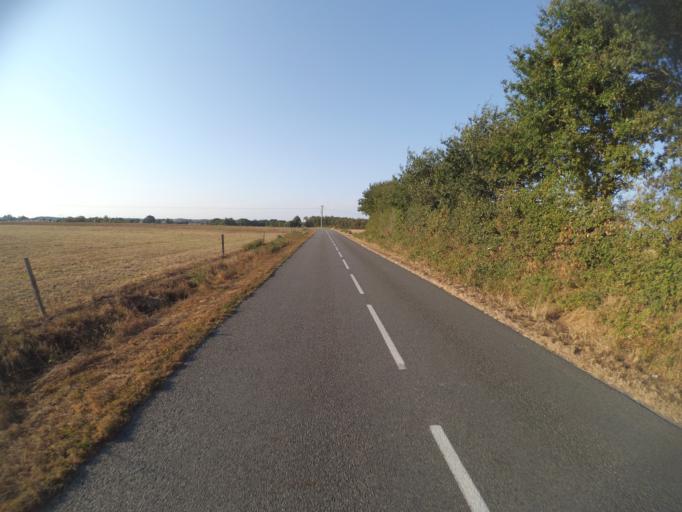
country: FR
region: Pays de la Loire
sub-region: Departement de la Loire-Atlantique
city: La Planche
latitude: 47.0171
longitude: -1.4233
